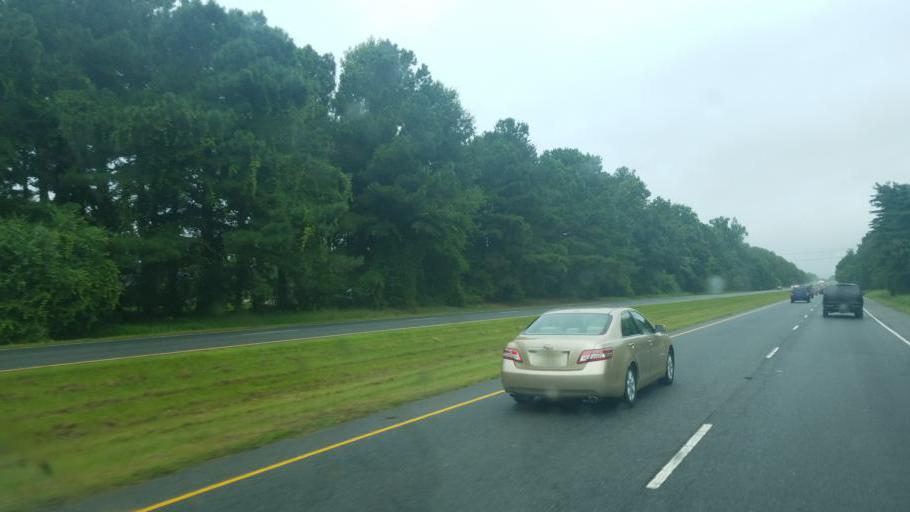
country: US
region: Virginia
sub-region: City of Chesapeake
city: Chesapeake
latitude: 36.6940
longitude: -76.2275
